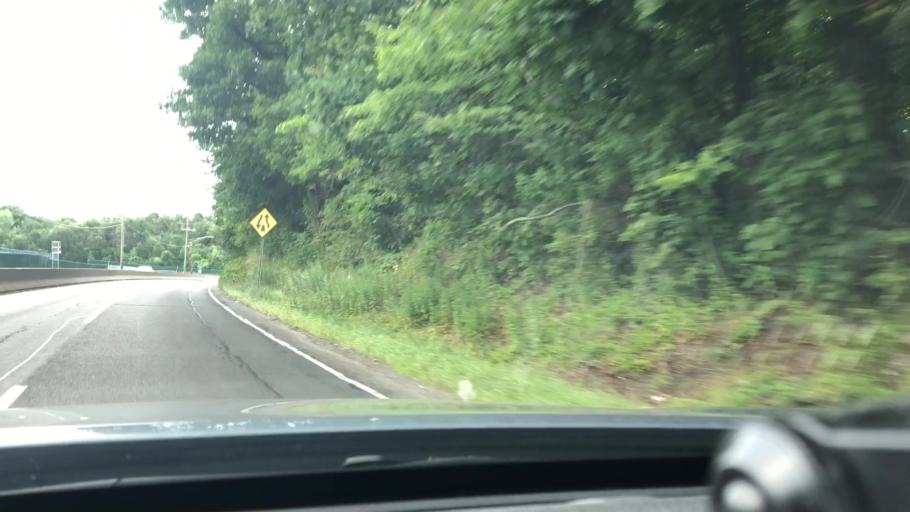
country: US
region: New York
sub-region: Rockland County
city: West Nyack
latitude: 41.0897
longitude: -73.9500
